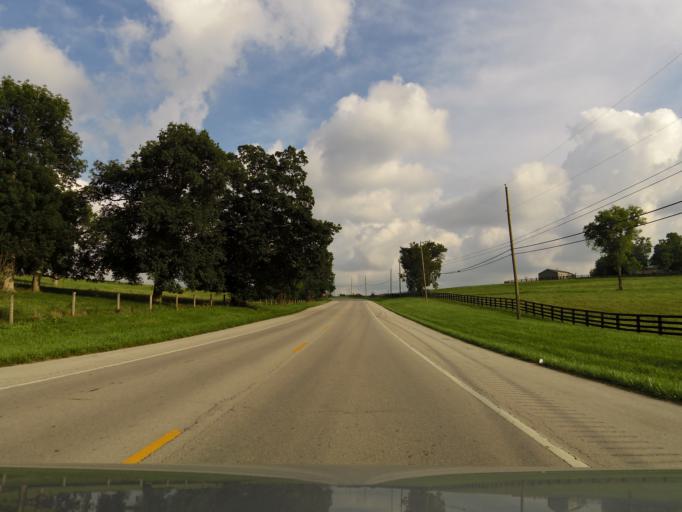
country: US
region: Kentucky
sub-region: Bourbon County
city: Paris
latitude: 38.2409
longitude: -84.2832
